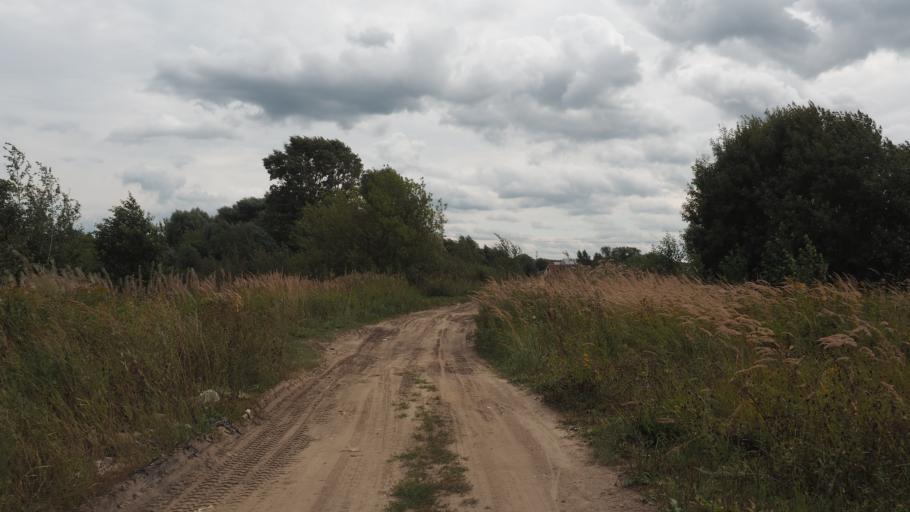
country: RU
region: Moskovskaya
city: Ramenskoye
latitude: 55.5581
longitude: 38.2934
